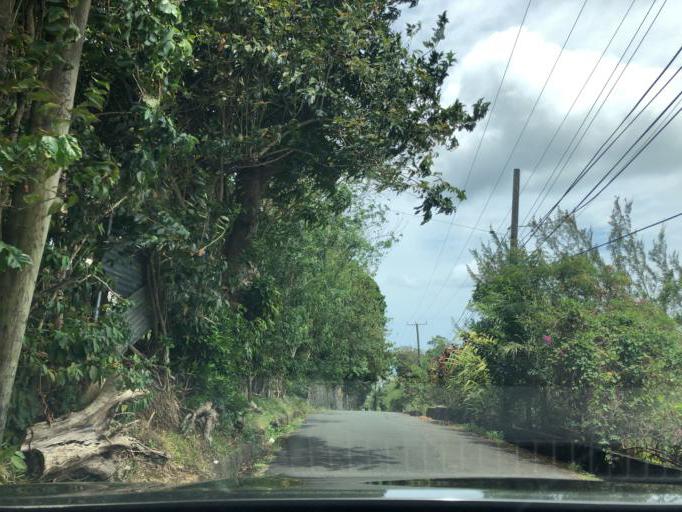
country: LC
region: Castries Quarter
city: Castries
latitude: 14.0019
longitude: -60.9957
